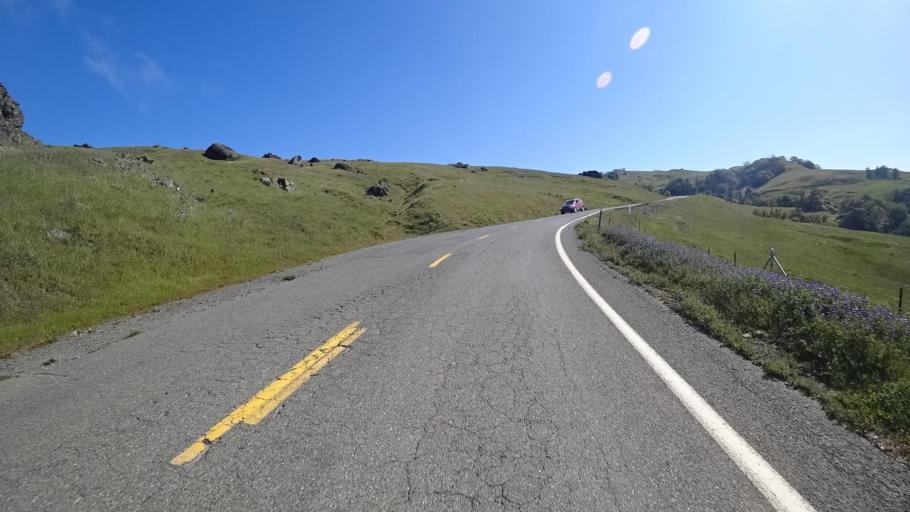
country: US
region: California
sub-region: Humboldt County
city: Redway
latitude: 40.1052
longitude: -123.7041
